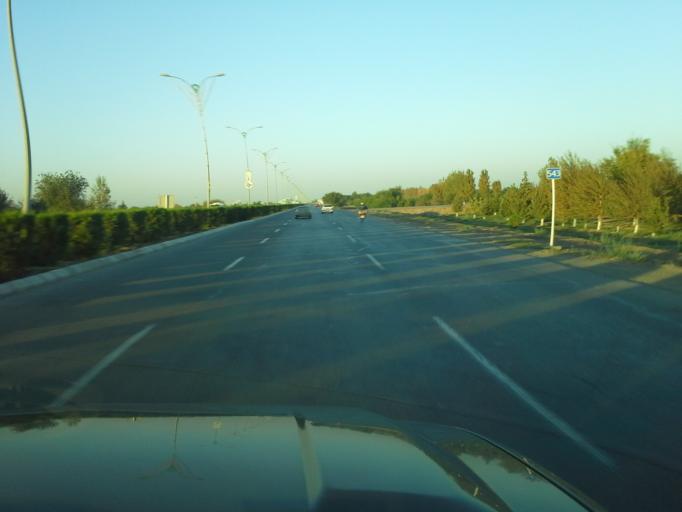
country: TM
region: Dasoguz
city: Dasoguz
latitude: 41.8009
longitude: 59.8977
